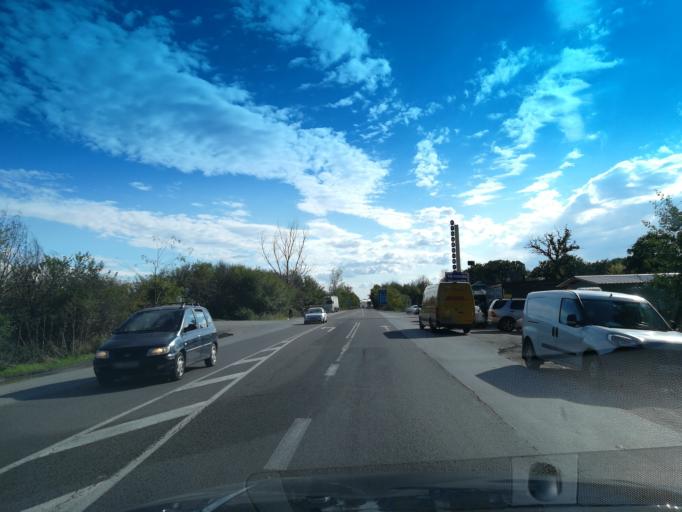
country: BG
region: Stara Zagora
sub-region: Obshtina Stara Zagora
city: Stara Zagora
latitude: 42.3497
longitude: 25.6589
